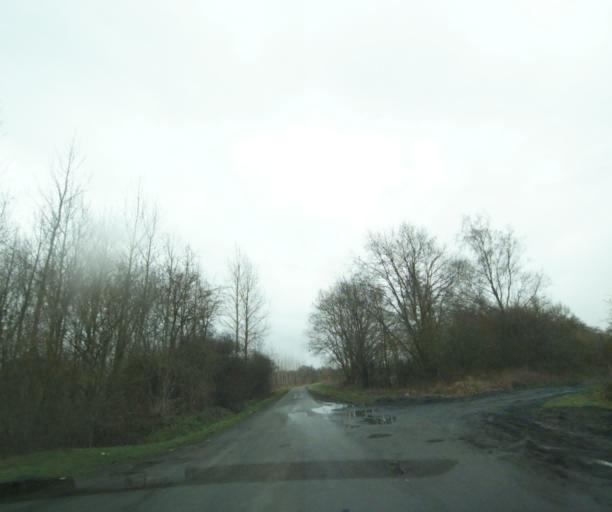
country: FR
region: Nord-Pas-de-Calais
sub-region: Departement du Nord
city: Vicq
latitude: 50.4216
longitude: 3.6243
